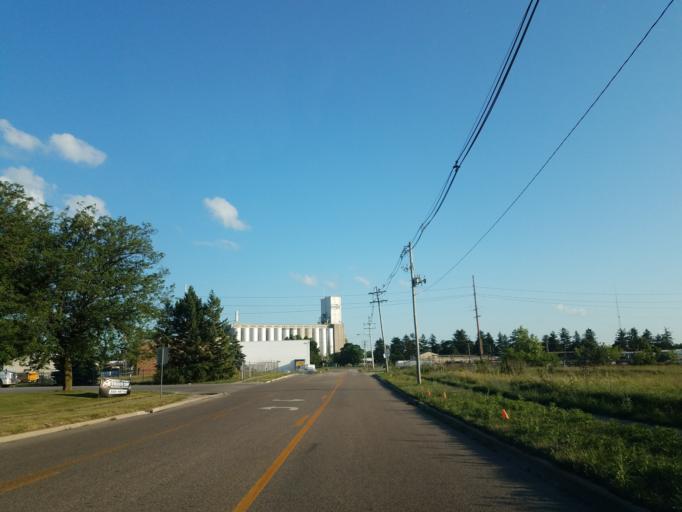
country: US
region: Illinois
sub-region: McLean County
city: Bloomington
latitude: 40.4814
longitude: -89.0185
